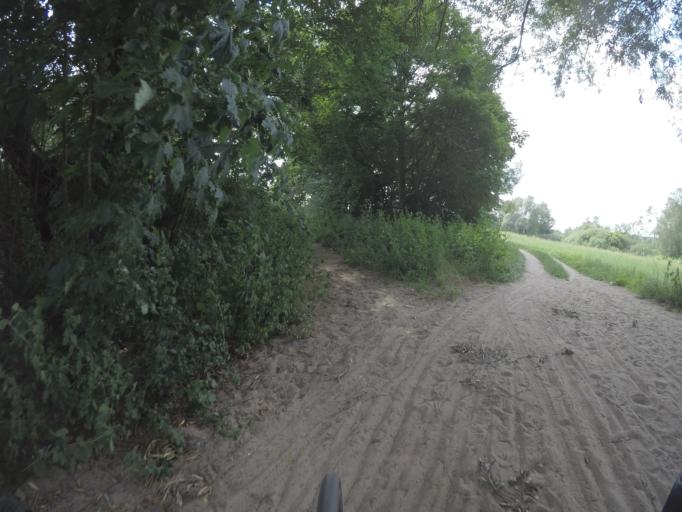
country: DE
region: Berlin
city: Lubars
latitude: 52.6207
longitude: 13.3671
